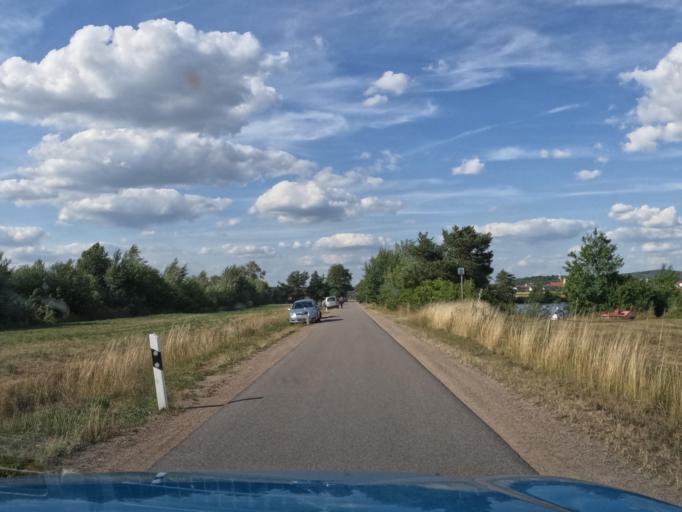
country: DE
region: Bavaria
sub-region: Upper Palatinate
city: Schwarzenfeld
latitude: 49.3780
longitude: 12.1202
